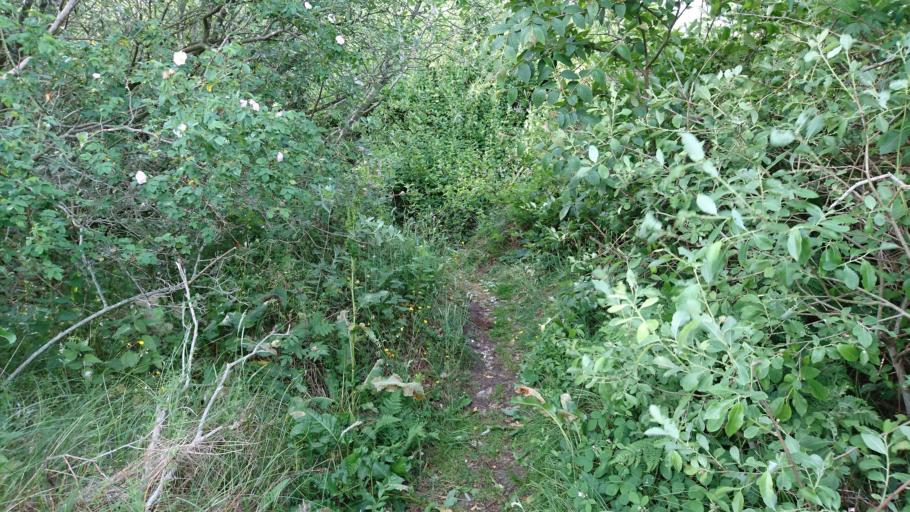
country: DK
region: North Denmark
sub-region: Frederikshavn Kommune
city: Skagen
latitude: 57.7423
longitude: 10.5933
